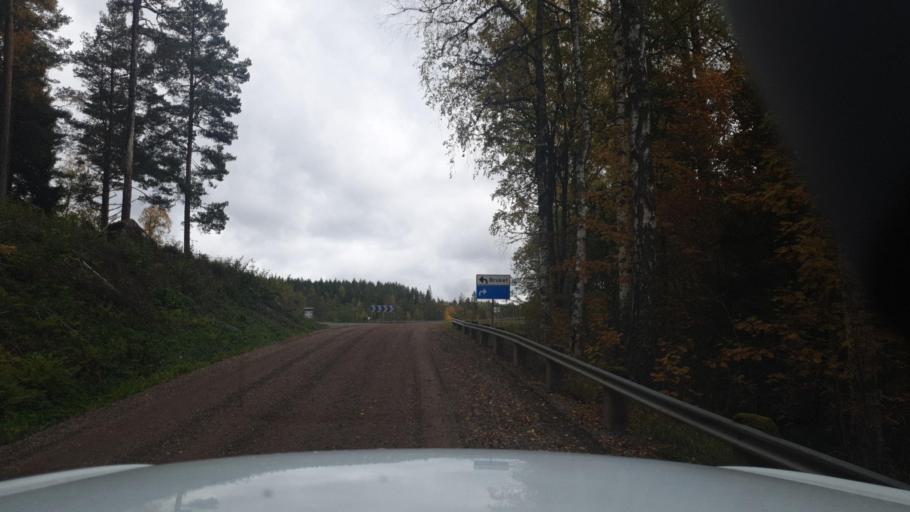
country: SE
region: Vaermland
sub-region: Eda Kommun
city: Charlottenberg
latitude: 60.0887
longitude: 12.5130
